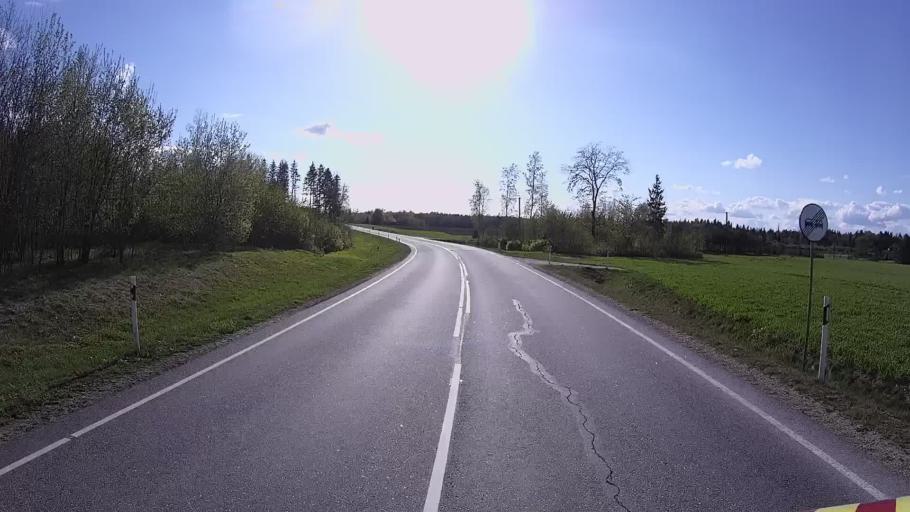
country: EE
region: Jogevamaa
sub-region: Poltsamaa linn
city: Poltsamaa
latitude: 58.6387
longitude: 25.7631
